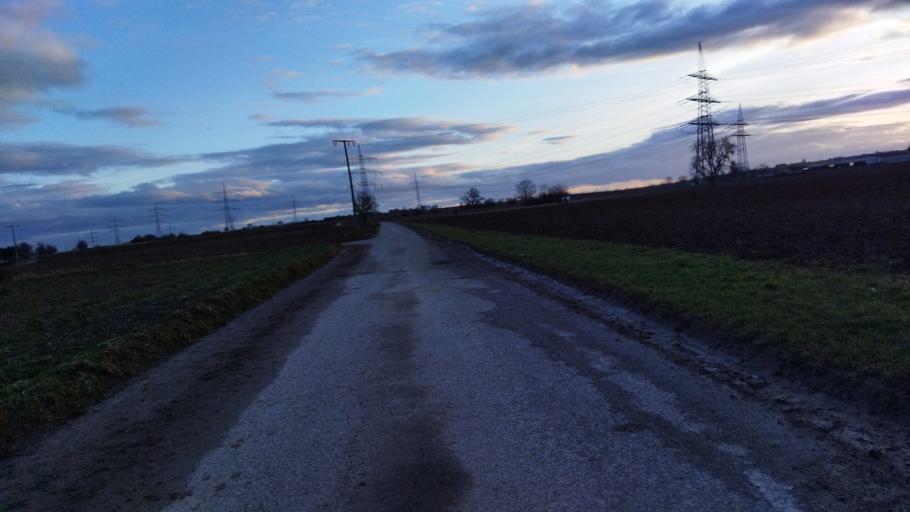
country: DE
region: Baden-Wuerttemberg
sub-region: Regierungsbezirk Stuttgart
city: Talheim
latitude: 49.1053
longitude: 9.1726
